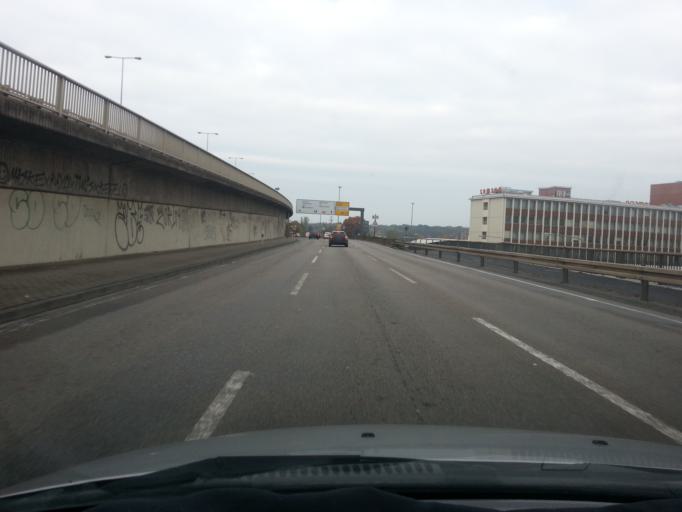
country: DE
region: Hesse
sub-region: Regierungsbezirk Darmstadt
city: Offenbach
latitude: 50.1166
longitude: 8.7327
